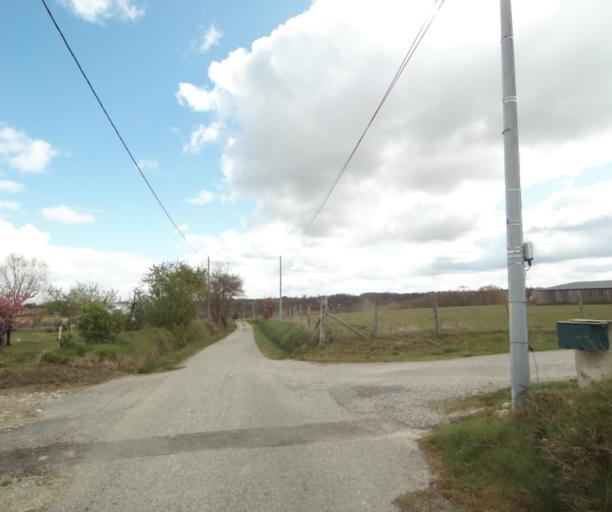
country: FR
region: Midi-Pyrenees
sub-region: Departement de l'Ariege
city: Saverdun
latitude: 43.2096
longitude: 1.5698
